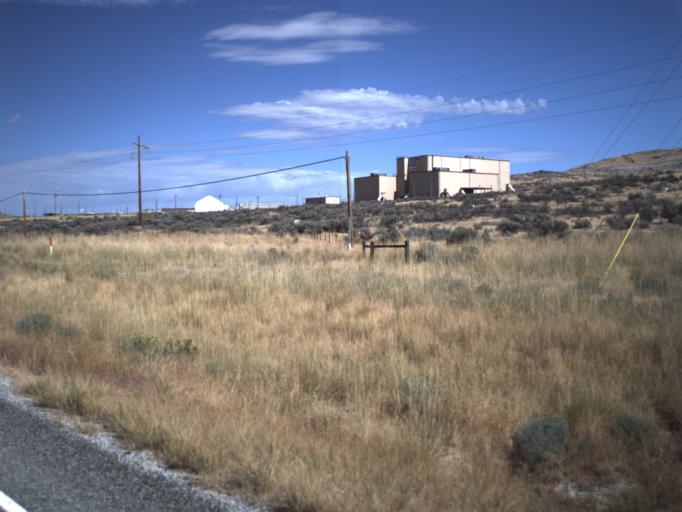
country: US
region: Utah
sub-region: Box Elder County
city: Tremonton
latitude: 41.6461
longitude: -112.4323
